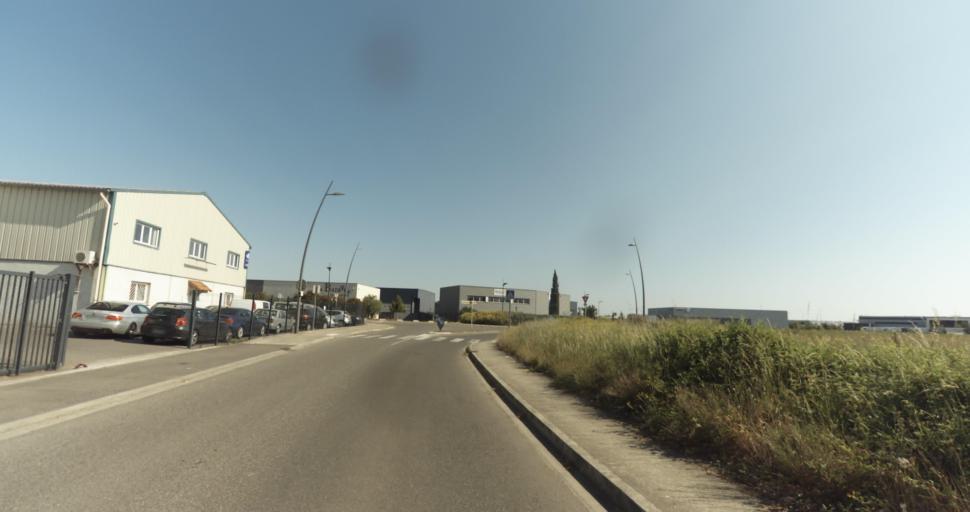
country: FR
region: Midi-Pyrenees
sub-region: Departement de la Haute-Garonne
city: Tournefeuille
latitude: 43.5908
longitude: 1.2988
